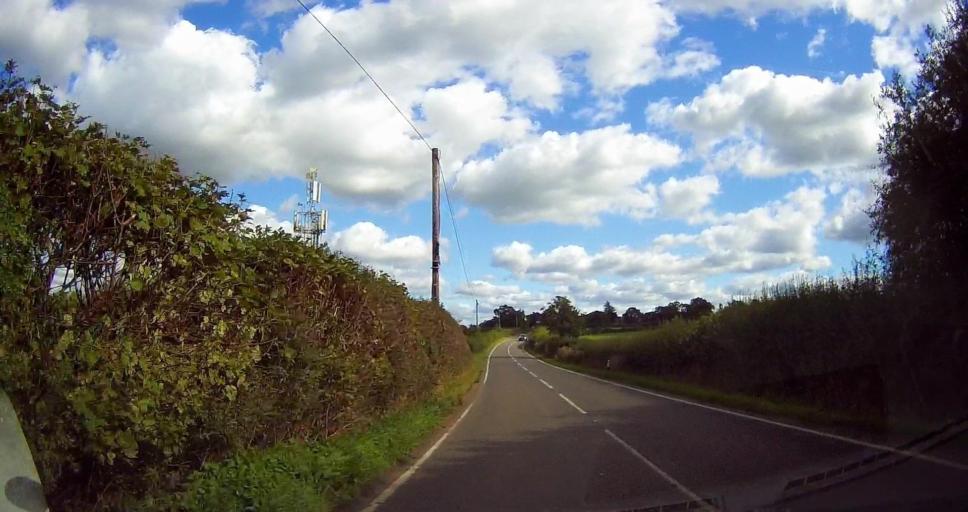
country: GB
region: England
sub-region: Cheshire East
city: Chorlton
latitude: 52.9815
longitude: -2.4326
